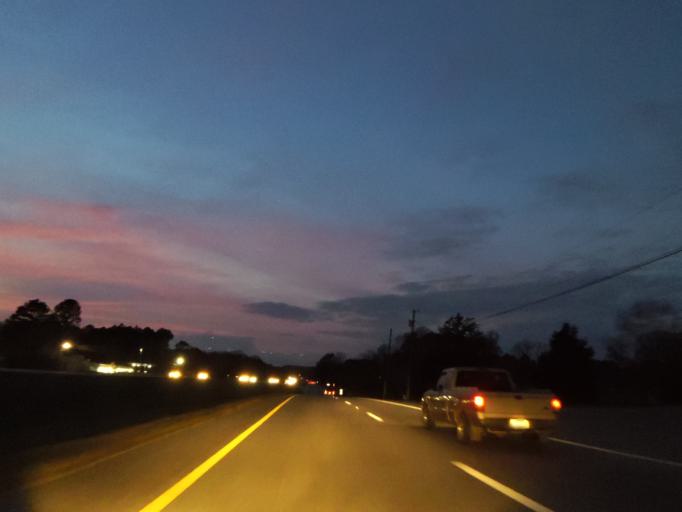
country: US
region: Tennessee
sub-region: Polk County
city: Benton
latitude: 35.1316
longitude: -84.7377
